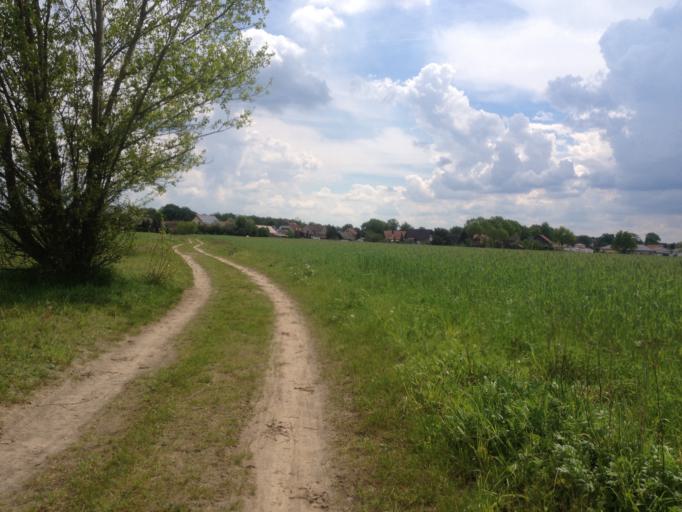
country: DE
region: Brandenburg
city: Drehnow
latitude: 51.8116
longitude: 14.3509
